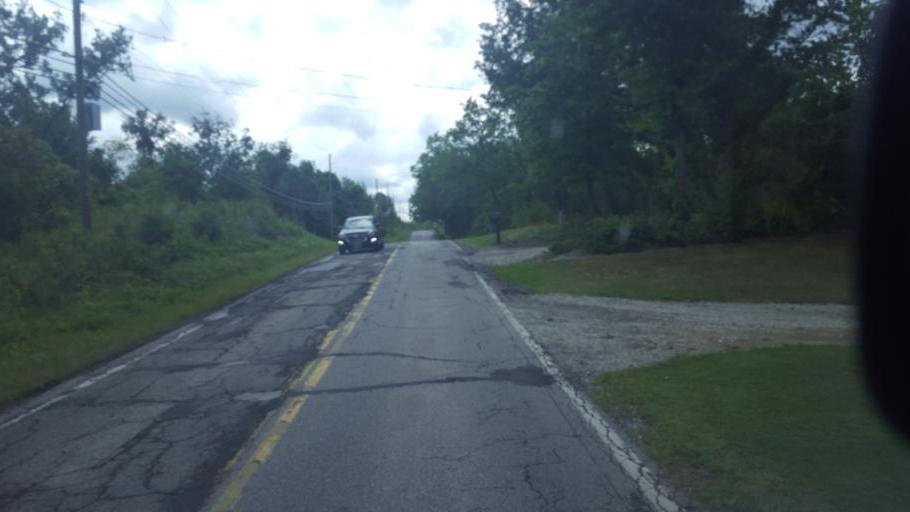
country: US
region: Ohio
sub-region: Lake County
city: Perry
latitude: 41.7178
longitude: -81.1792
